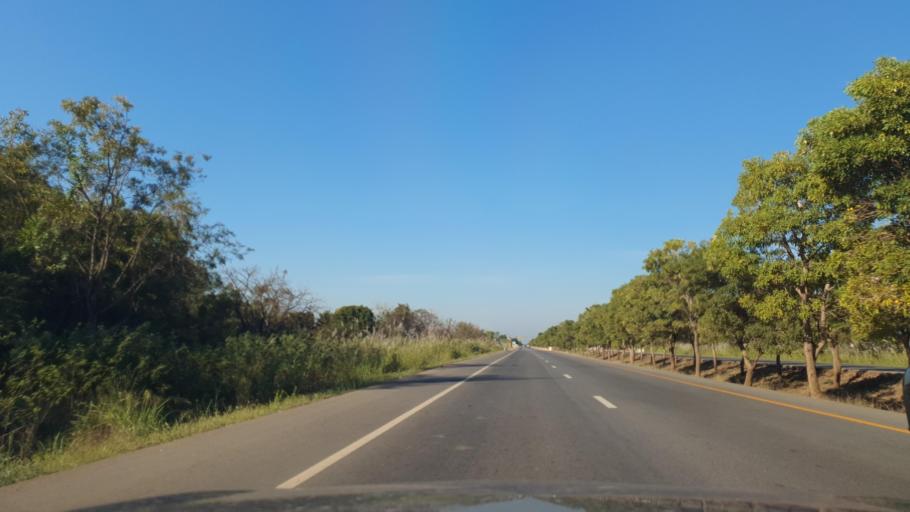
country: TH
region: Sukhothai
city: Sukhothai
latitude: 17.0692
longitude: 99.7989
